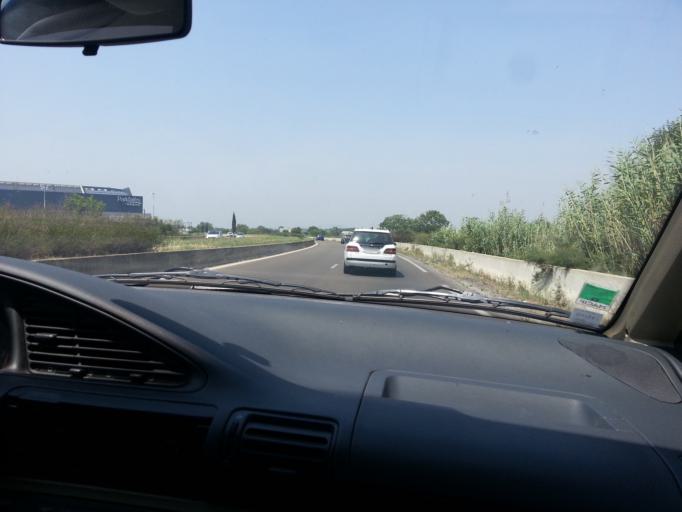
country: FR
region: Languedoc-Roussillon
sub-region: Departement de l'Herault
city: Perols
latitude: 43.5715
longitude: 3.9555
